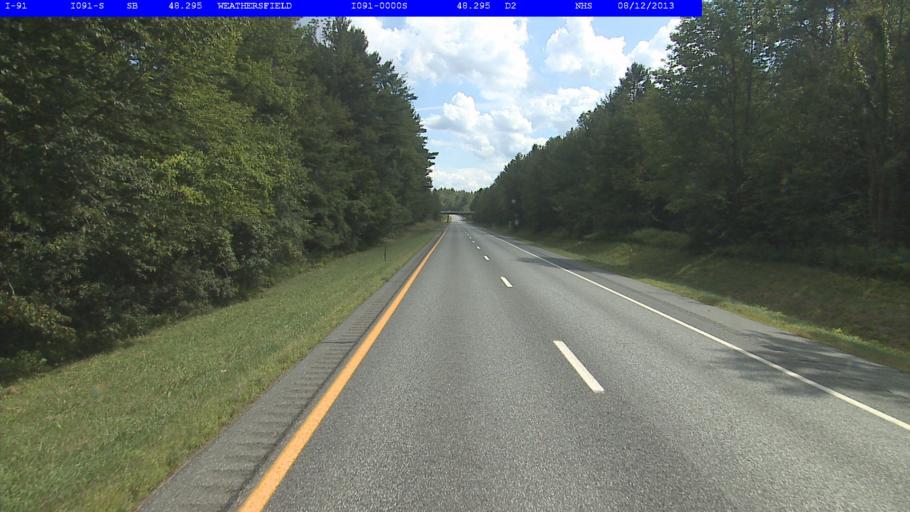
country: US
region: New Hampshire
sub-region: Sullivan County
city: Claremont
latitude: 43.3593
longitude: -72.4241
